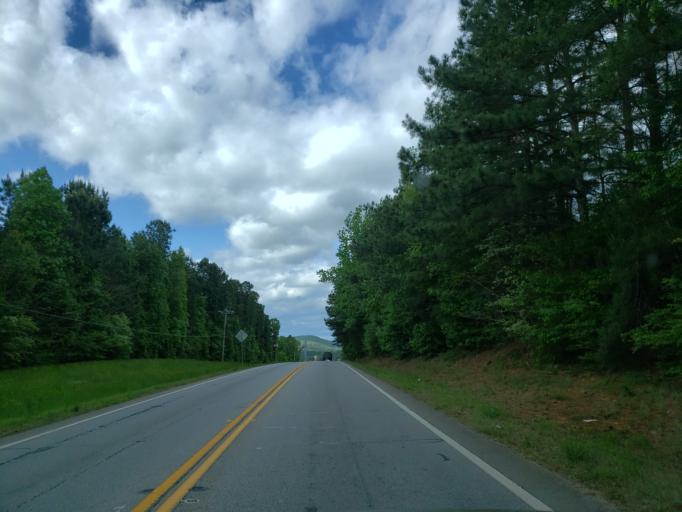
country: US
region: Georgia
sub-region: Haralson County
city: Tallapoosa
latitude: 33.6736
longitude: -85.2634
